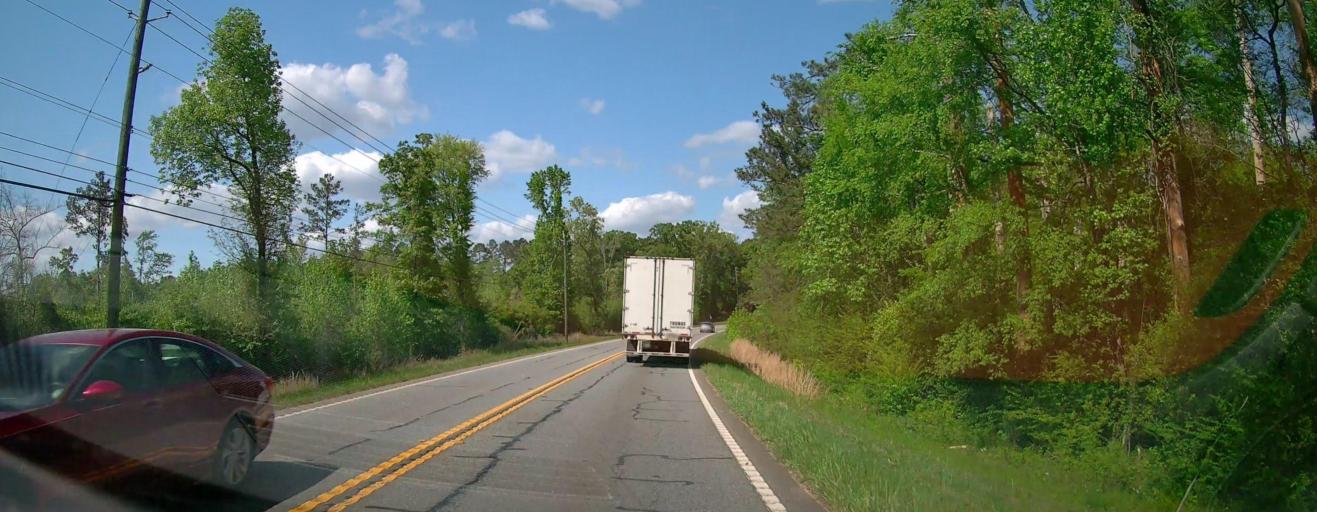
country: US
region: Georgia
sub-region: Greene County
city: Greensboro
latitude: 33.5319
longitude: -83.2195
